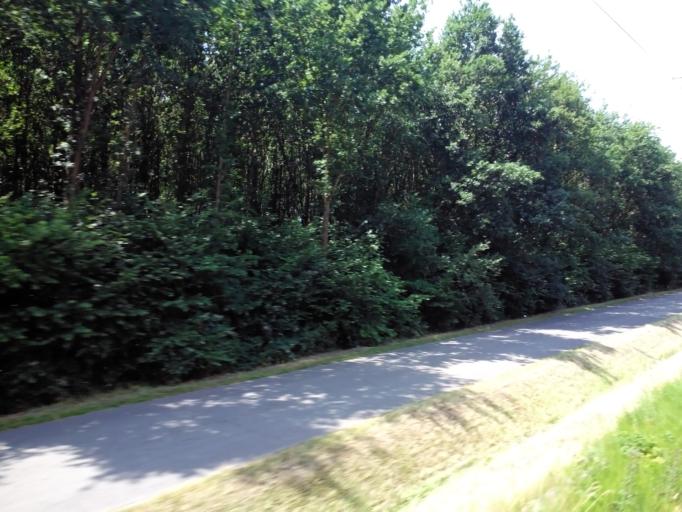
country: BE
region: Flanders
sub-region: Provincie Antwerpen
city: Lier
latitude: 51.1431
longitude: 4.5334
